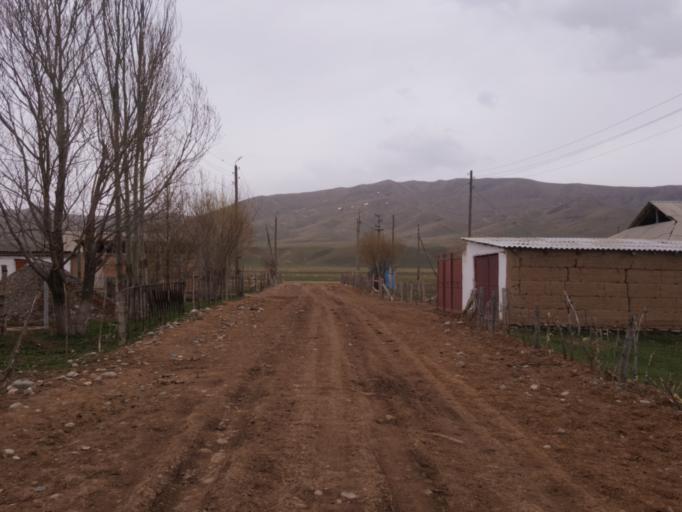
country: KG
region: Naryn
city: Naryn
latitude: 41.5194
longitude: 76.4397
